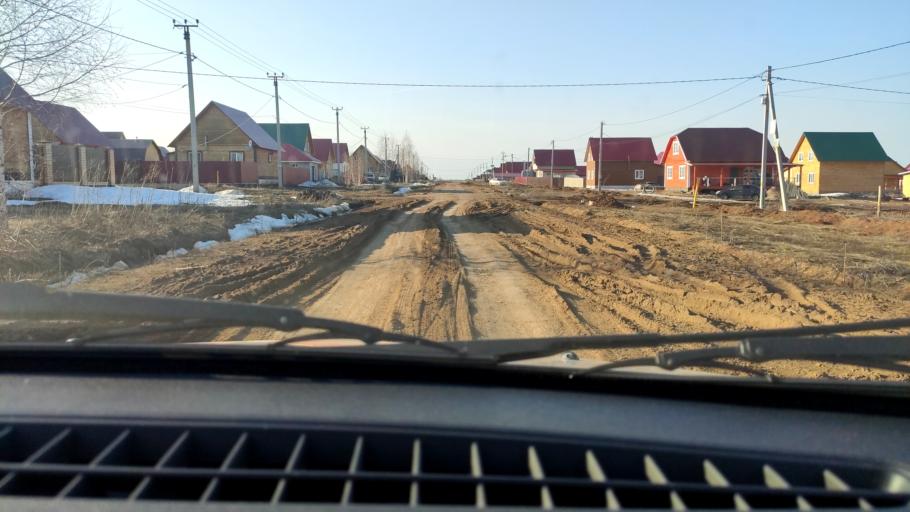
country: RU
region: Bashkortostan
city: Iglino
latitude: 54.8187
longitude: 56.4437
